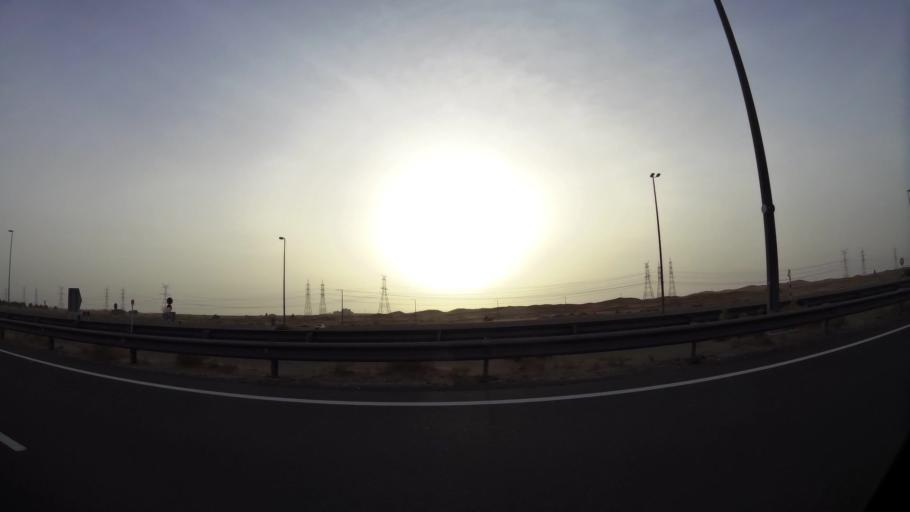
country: OM
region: Al Buraimi
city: Al Buraymi
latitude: 24.2923
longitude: 55.7372
